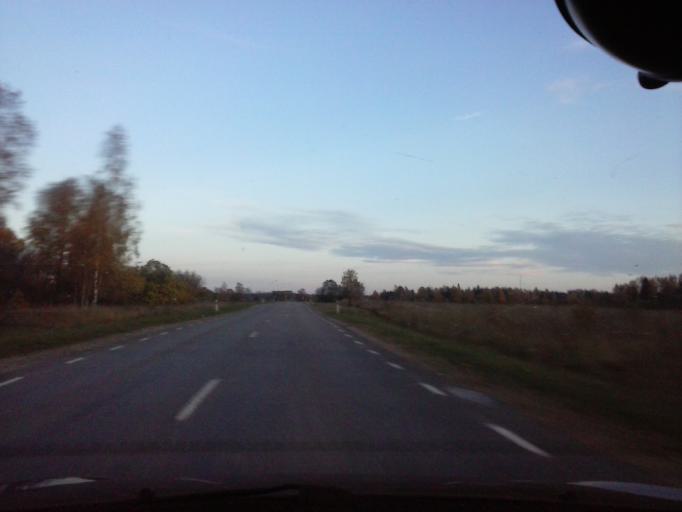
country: EE
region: Raplamaa
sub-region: Maerjamaa vald
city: Marjamaa
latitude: 58.9248
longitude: 24.3970
